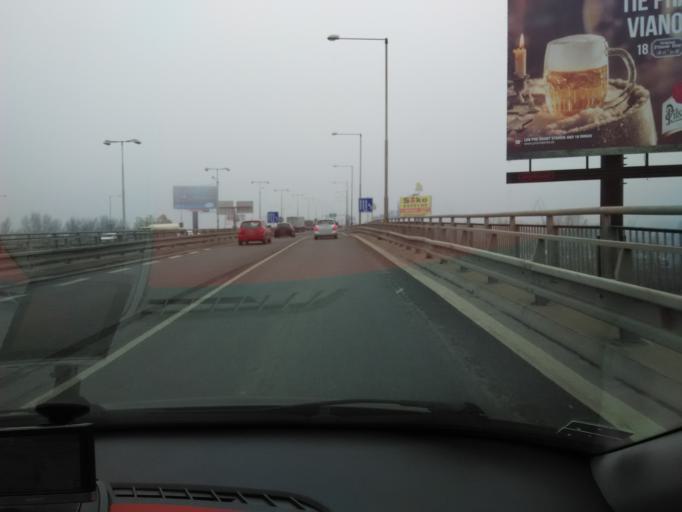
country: SK
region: Bratislavsky
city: Bratislava
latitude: 48.1408
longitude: 17.1477
